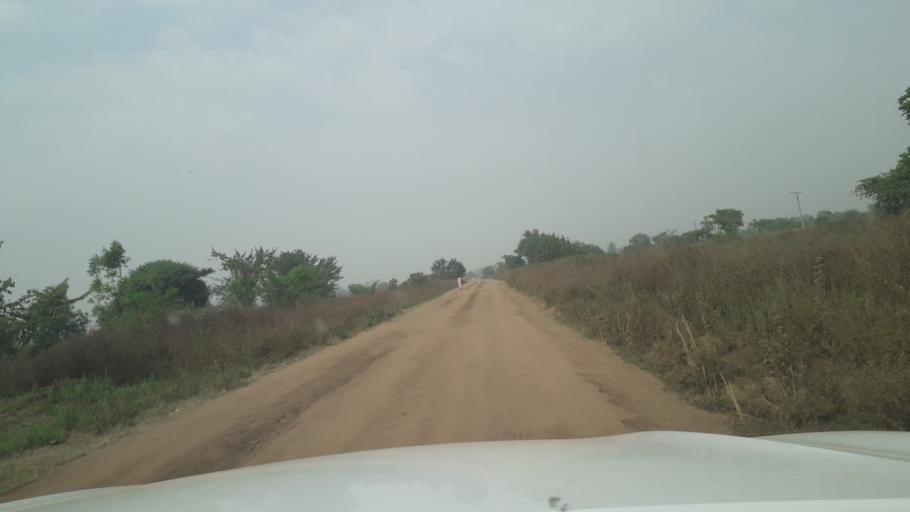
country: ET
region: Gambela
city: Gambela
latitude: 8.3287
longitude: 33.7351
